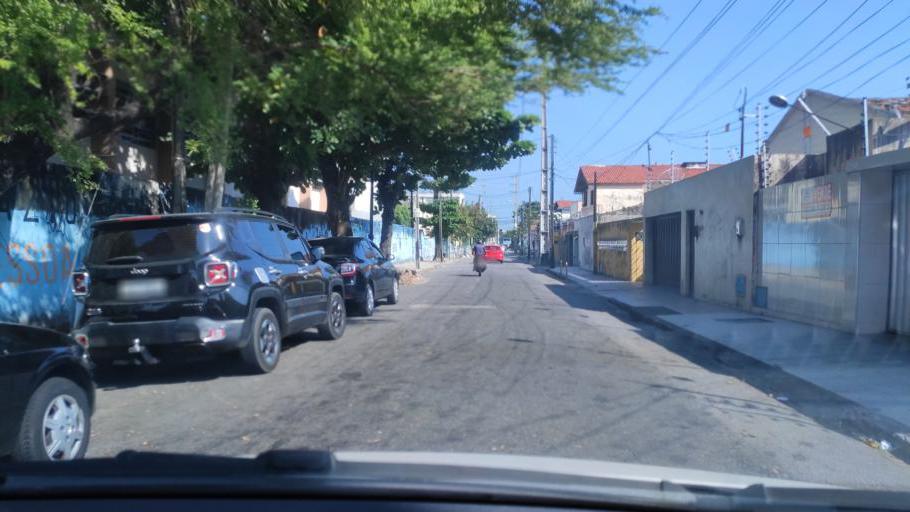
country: BR
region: Ceara
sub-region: Fortaleza
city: Fortaleza
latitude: -3.7414
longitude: -38.5363
